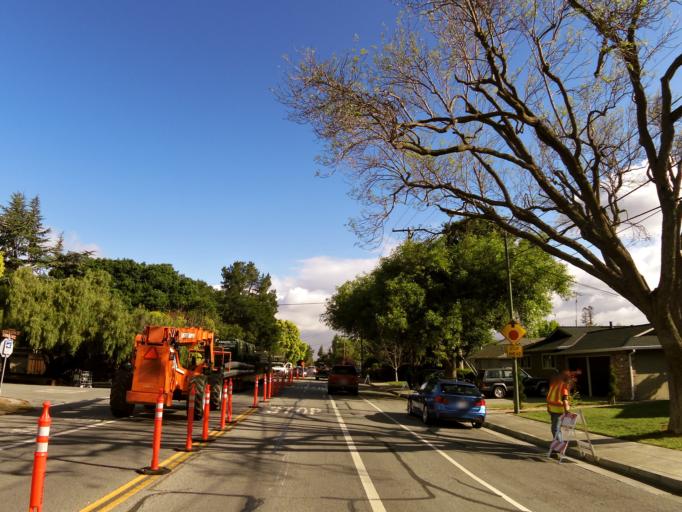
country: US
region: California
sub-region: Santa Clara County
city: Mountain View
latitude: 37.3726
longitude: -122.0960
